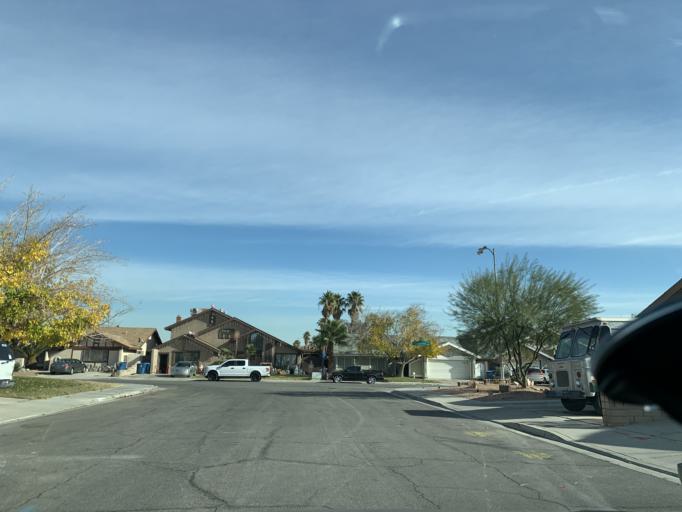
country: US
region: Nevada
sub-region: Clark County
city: Spring Valley
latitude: 36.1084
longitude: -115.2351
